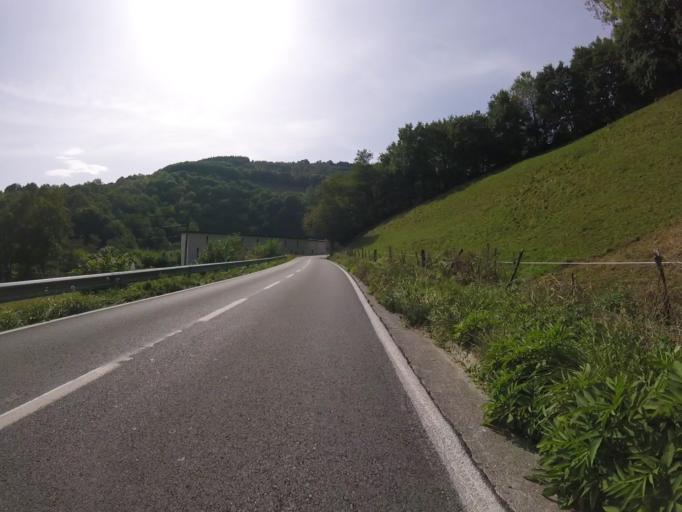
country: ES
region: Navarre
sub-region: Provincia de Navarra
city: Elgorriaga
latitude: 43.1362
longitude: -1.6905
